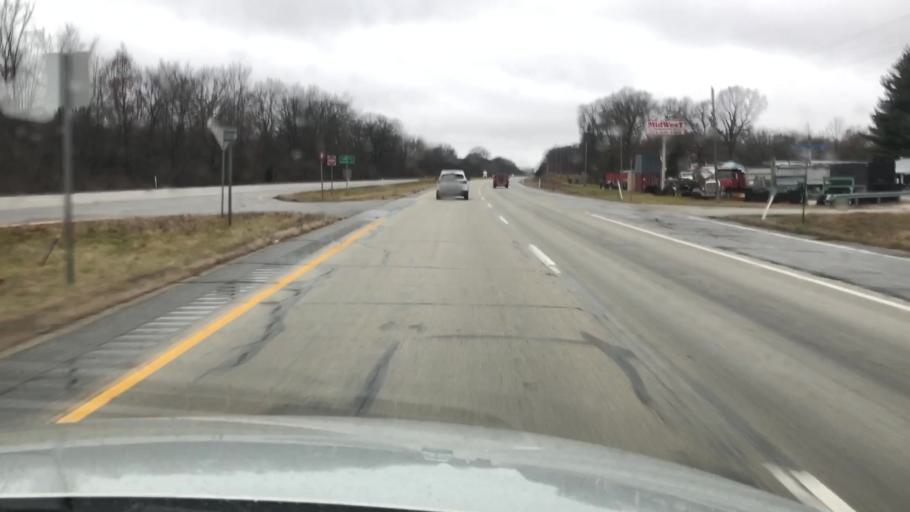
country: US
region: Indiana
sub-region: Starke County
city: Koontz Lake
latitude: 41.3648
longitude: -86.4660
